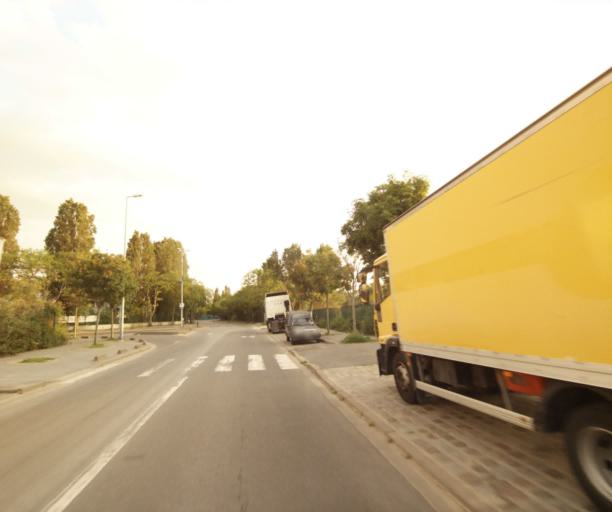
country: FR
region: Ile-de-France
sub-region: Departement des Hauts-de-Seine
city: Villeneuve-la-Garenne
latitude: 48.9332
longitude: 2.3130
